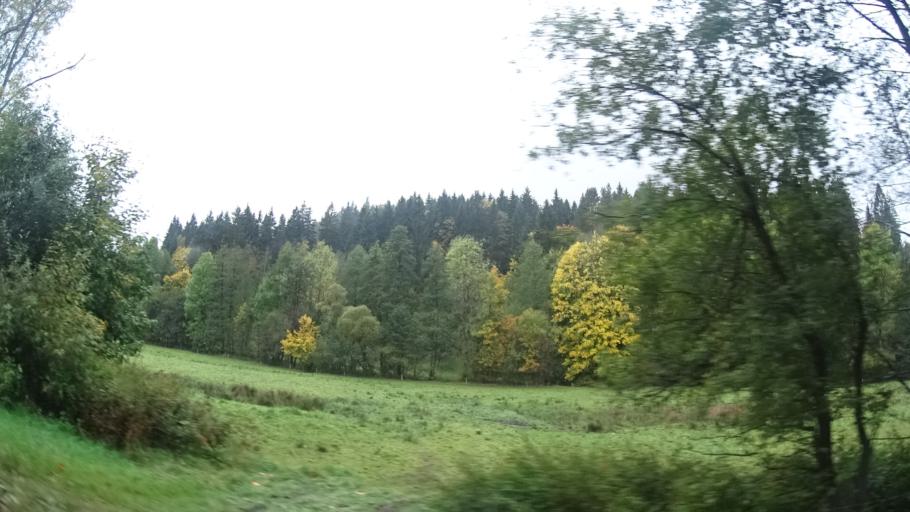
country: DE
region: Thuringia
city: Wurzbach
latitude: 50.4861
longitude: 11.5488
